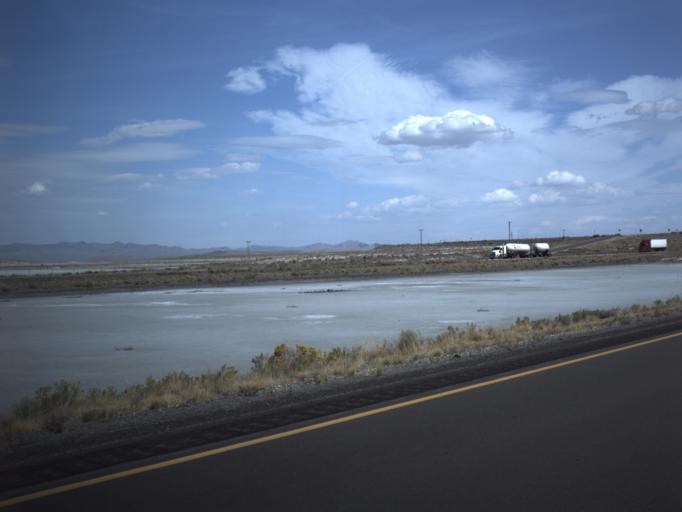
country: US
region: Utah
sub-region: Tooele County
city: Wendover
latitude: 40.7265
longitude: -113.2646
